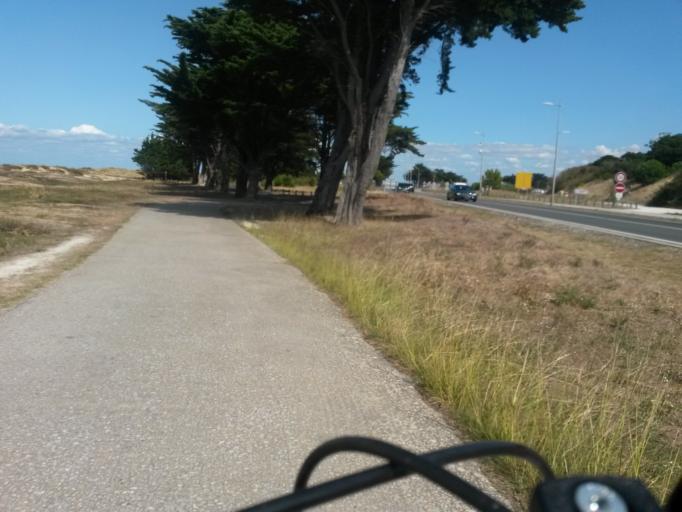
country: FR
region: Poitou-Charentes
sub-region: Departement de la Charente-Maritime
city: Rivedoux-Plage
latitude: 46.1612
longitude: -1.2615
